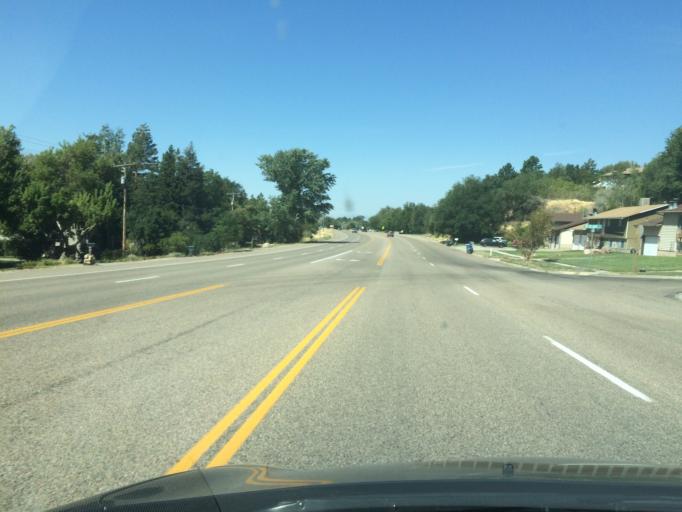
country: US
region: Utah
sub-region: Weber County
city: Ogden
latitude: 41.2398
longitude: -111.9361
